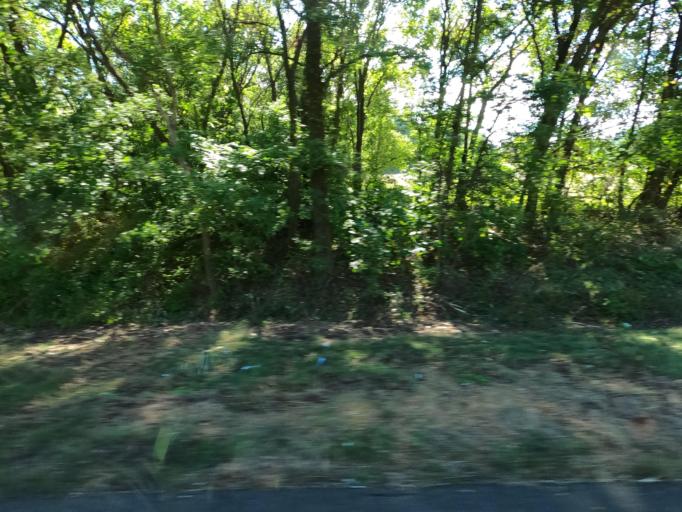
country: US
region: Tennessee
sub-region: Tipton County
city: Munford
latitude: 35.4321
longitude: -89.8064
